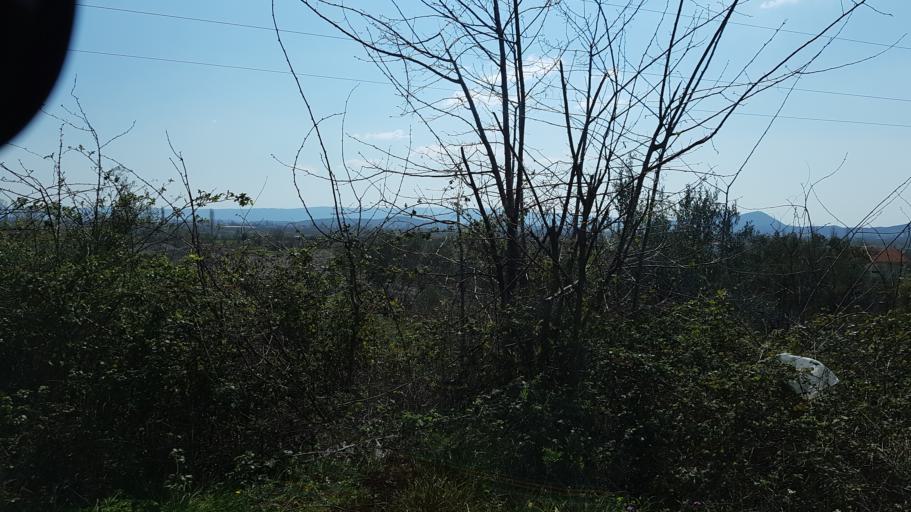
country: AL
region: Shkoder
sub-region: Rrethi i Shkodres
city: Vau i Dejes
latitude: 42.0099
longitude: 19.5928
